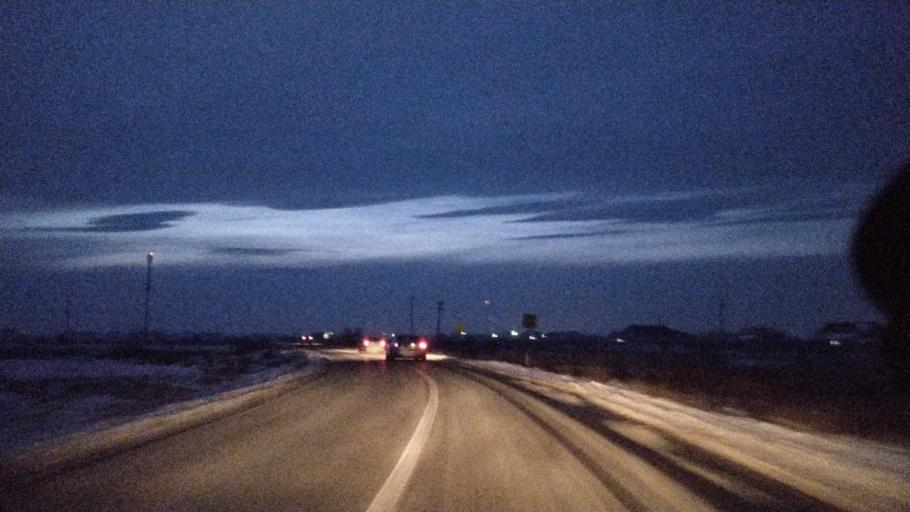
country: RO
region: Vrancea
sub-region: Comuna Milcovul
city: Milcovul
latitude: 45.6770
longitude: 27.2507
